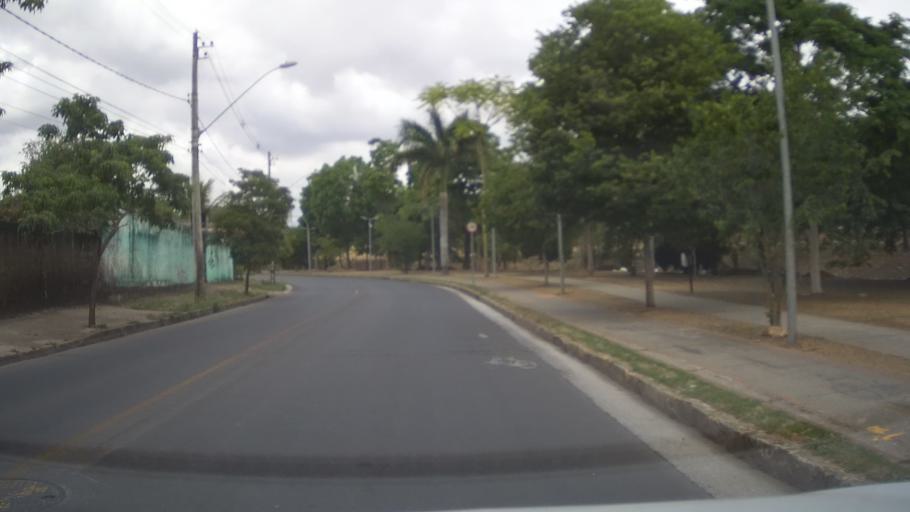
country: BR
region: Minas Gerais
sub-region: Belo Horizonte
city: Belo Horizonte
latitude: -19.8576
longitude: -43.9951
